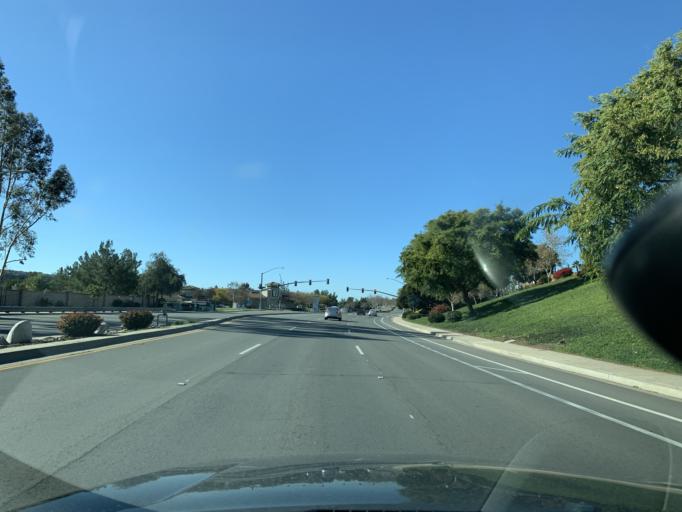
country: US
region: California
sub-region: San Diego County
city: Poway
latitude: 32.9457
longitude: -117.0823
